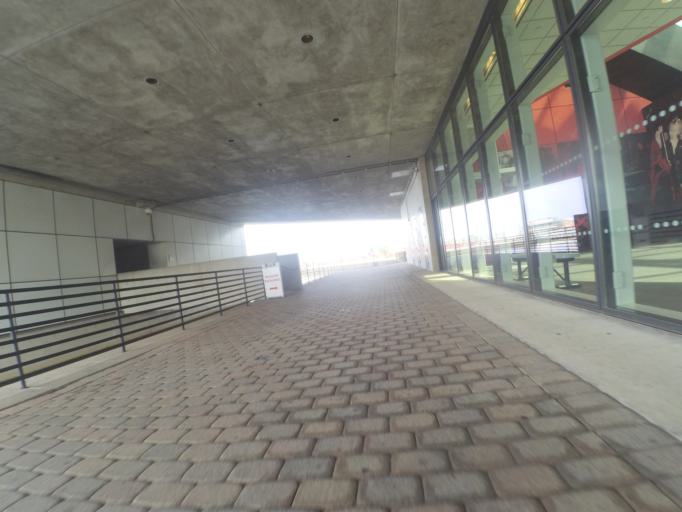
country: US
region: Ohio
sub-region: Cuyahoga County
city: Cleveland
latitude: 41.5084
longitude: -81.6954
